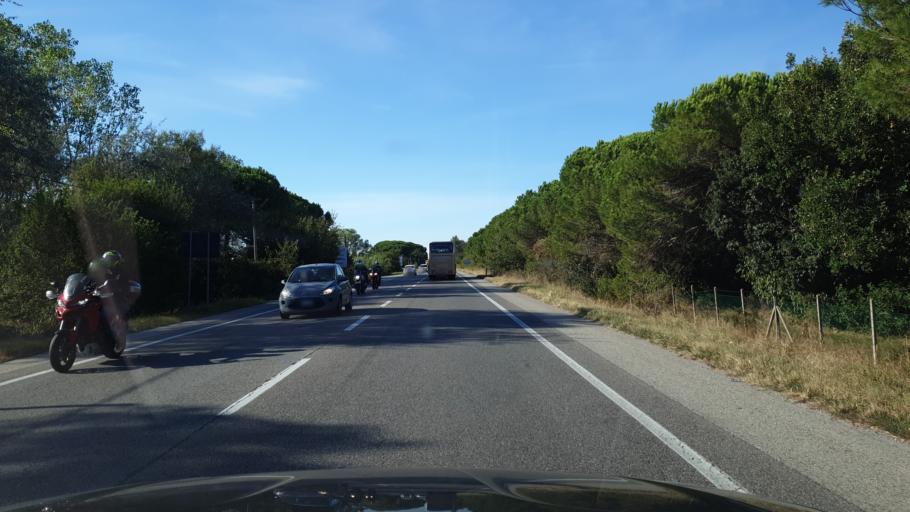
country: IT
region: Emilia-Romagna
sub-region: Provincia di Ravenna
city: Cervia
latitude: 44.2763
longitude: 12.3218
